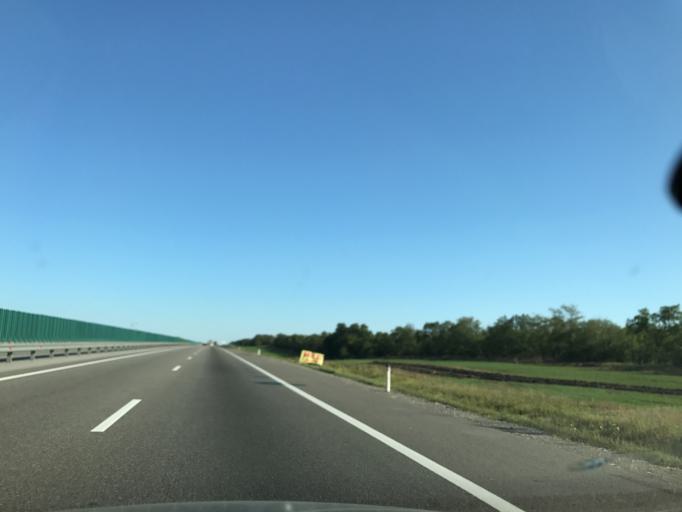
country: RU
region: Rostov
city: Glubokiy
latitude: 48.6120
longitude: 40.3548
